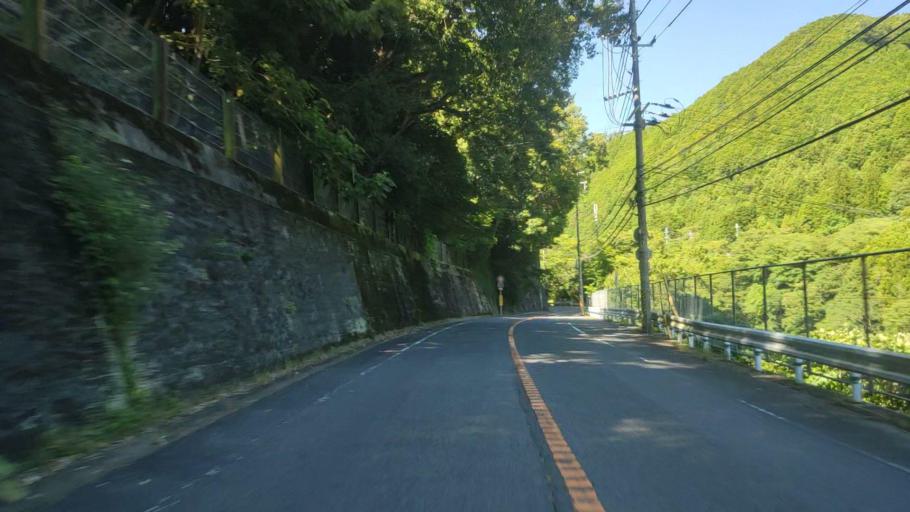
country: JP
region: Nara
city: Yoshino-cho
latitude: 34.3814
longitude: 135.9159
